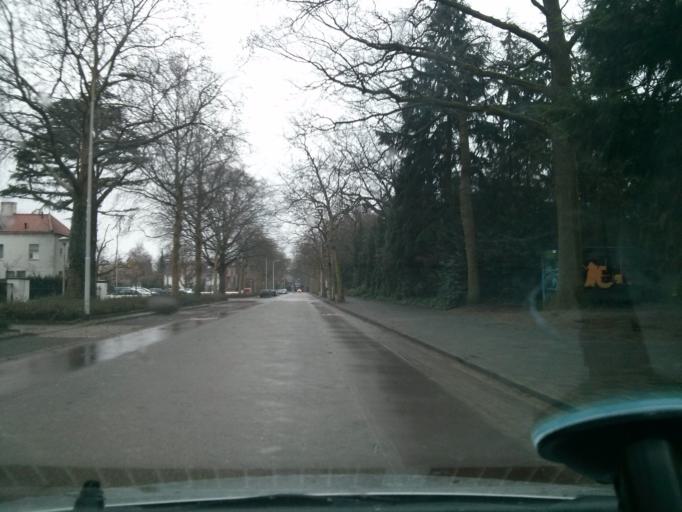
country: NL
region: North Brabant
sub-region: Gemeente Eindhoven
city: Eindhoven
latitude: 51.4261
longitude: 5.4799
